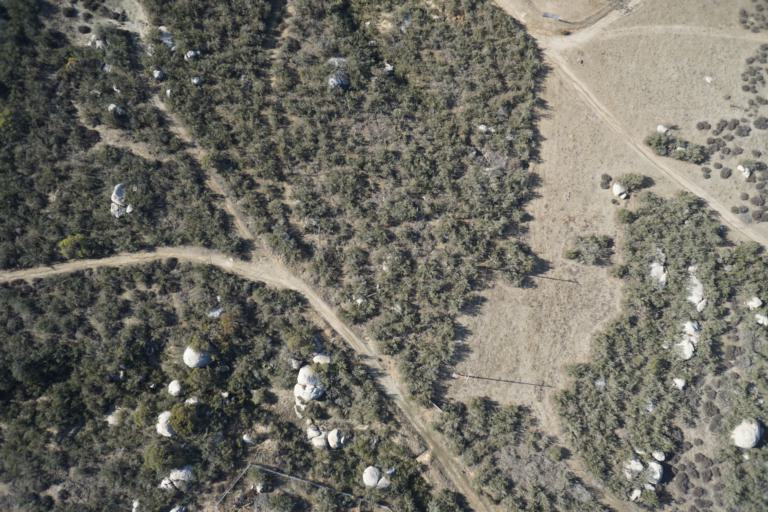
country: US
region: California
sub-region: Riverside County
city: East Hemet
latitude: 33.6248
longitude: -116.8964
